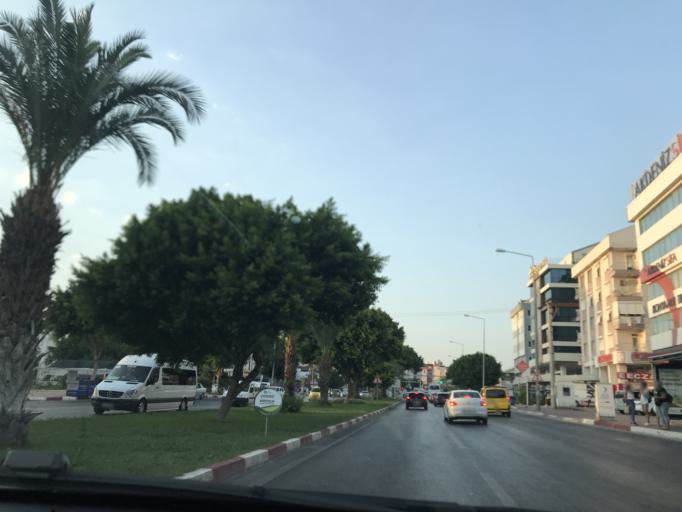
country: TR
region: Antalya
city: Antalya
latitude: 36.8731
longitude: 30.6421
